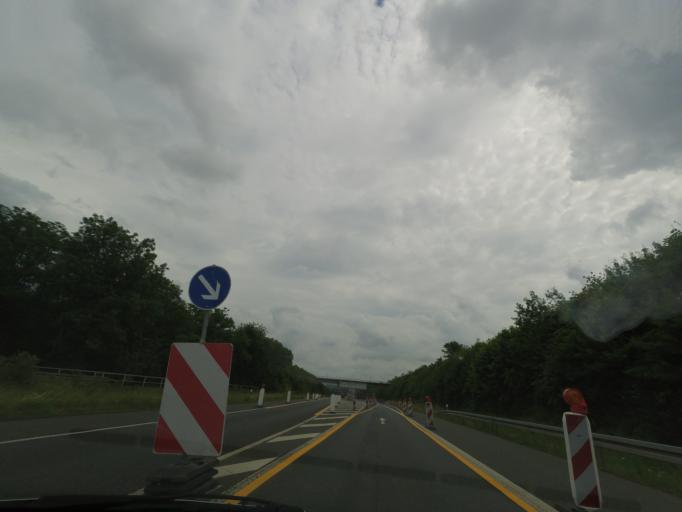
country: DE
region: Hesse
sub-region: Regierungsbezirk Giessen
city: Heuchelheim
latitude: 50.6048
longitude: 8.6411
